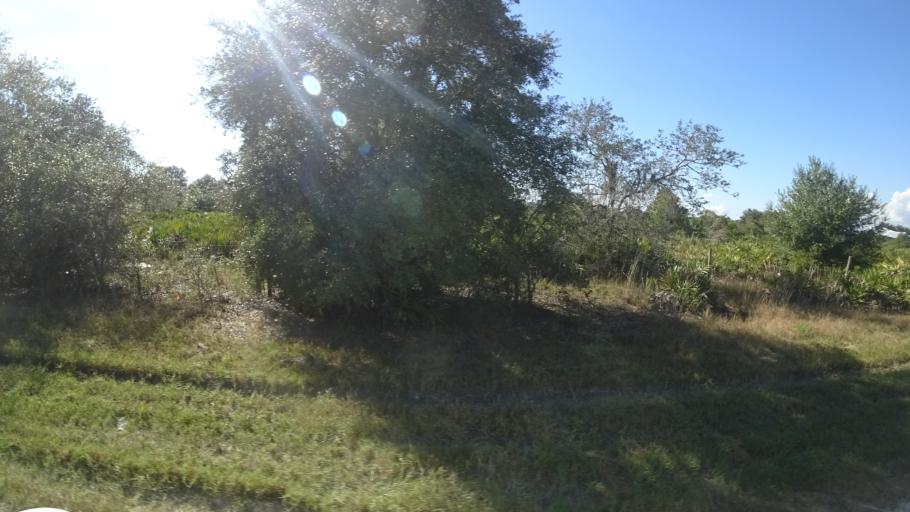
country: US
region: Florida
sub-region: Sarasota County
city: The Meadows
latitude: 27.4241
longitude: -82.2613
